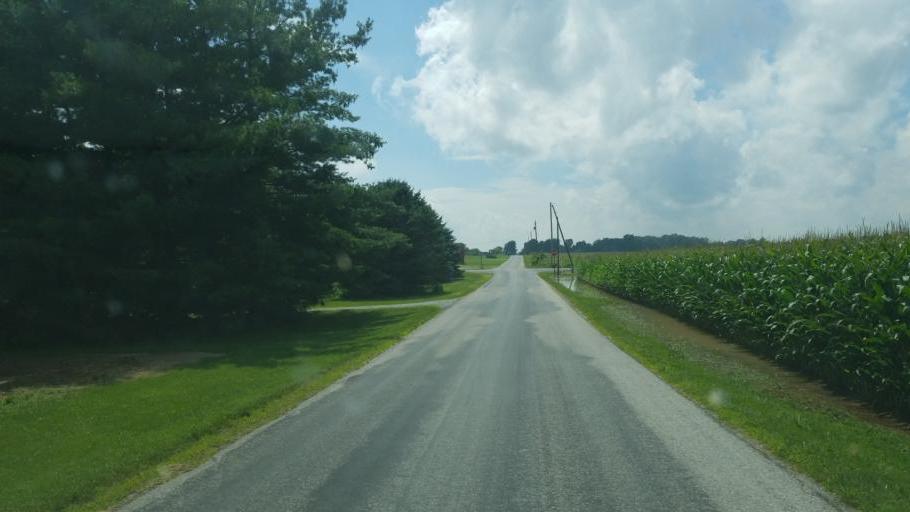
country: US
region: Ohio
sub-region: Union County
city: Richwood
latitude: 40.5604
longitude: -83.3908
